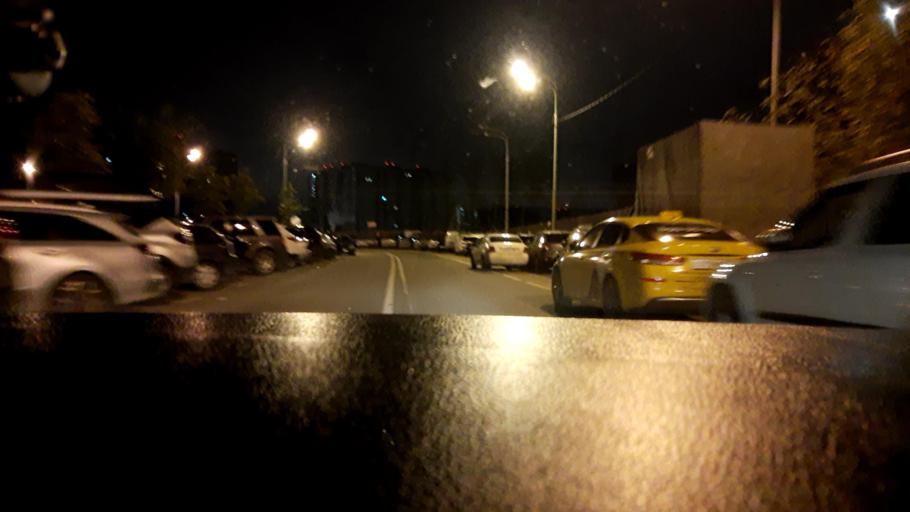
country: RU
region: Moscow
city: Khimki
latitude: 55.8718
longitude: 37.3918
